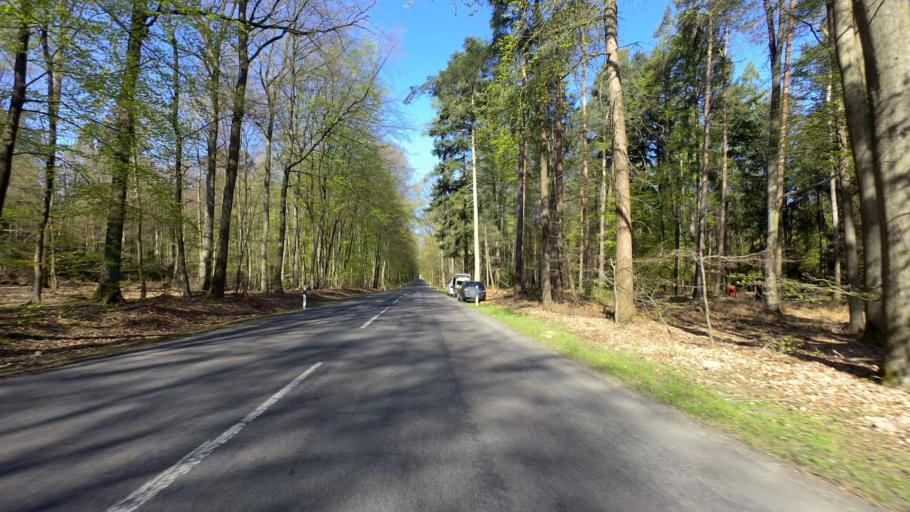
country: DE
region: Lower Saxony
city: Stockse
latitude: 52.6368
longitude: 9.3167
